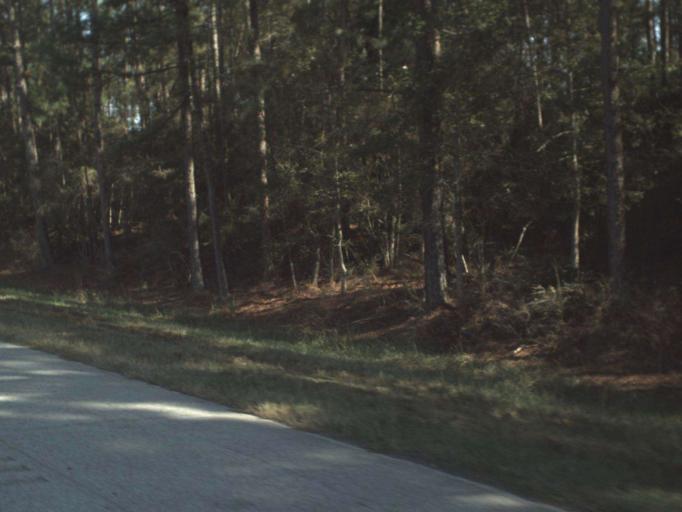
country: US
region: Florida
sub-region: Holmes County
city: Bonifay
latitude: 30.7599
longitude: -85.7996
